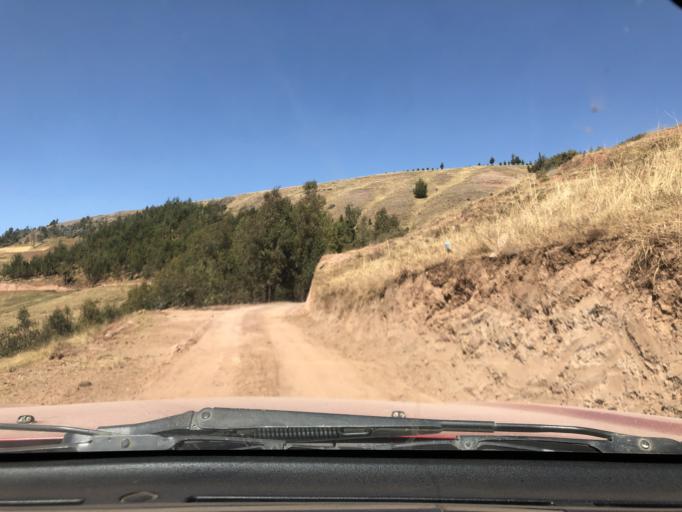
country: PE
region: Ayacucho
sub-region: Provincia de La Mar
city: Chilcas
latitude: -13.1812
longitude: -73.8455
